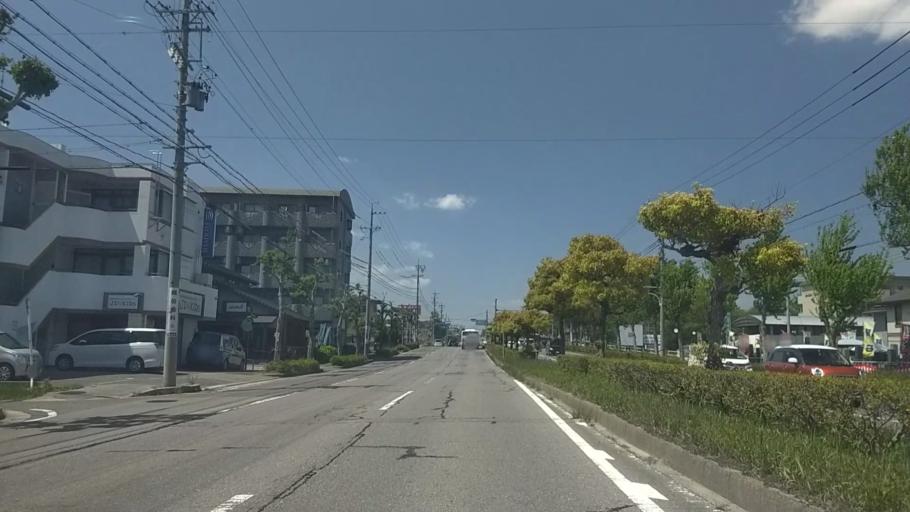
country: JP
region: Aichi
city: Okazaki
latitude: 34.9662
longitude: 137.1829
